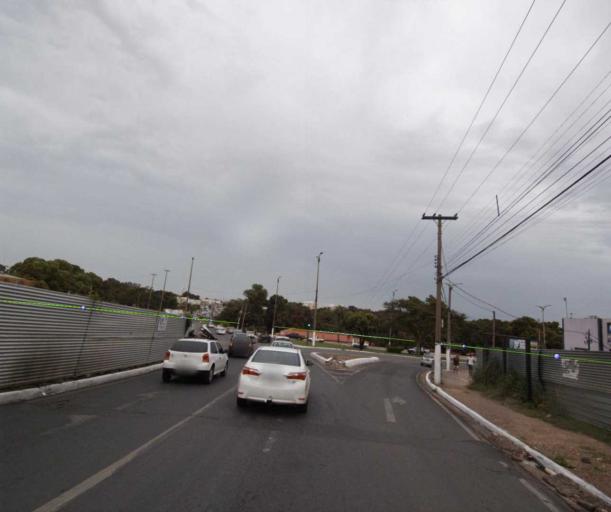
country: BR
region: Mato Grosso
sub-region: Cuiaba
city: Cuiaba
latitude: -15.6243
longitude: -56.0621
